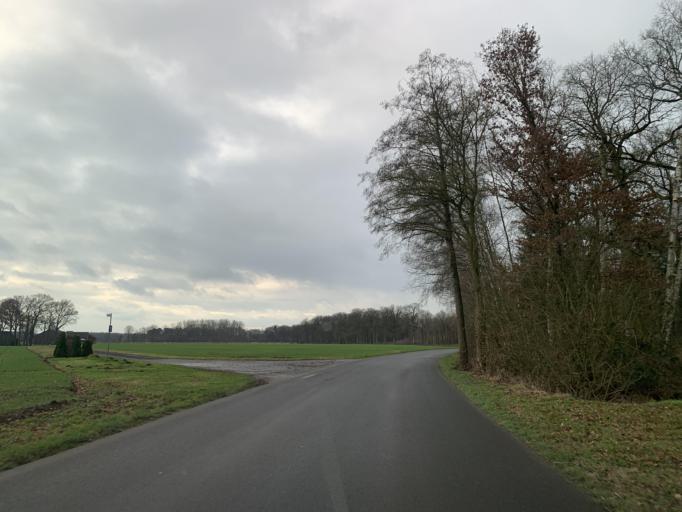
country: DE
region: North Rhine-Westphalia
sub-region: Regierungsbezirk Munster
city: Senden
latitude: 51.8927
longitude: 7.4807
